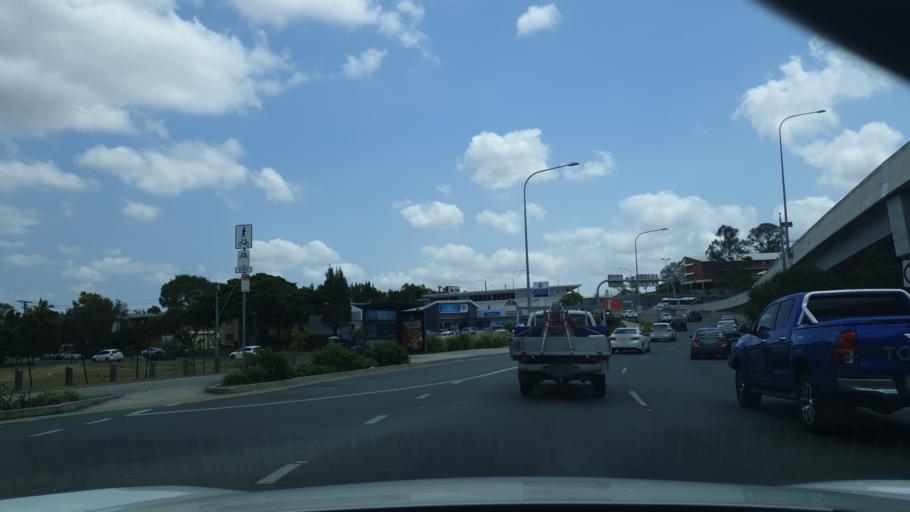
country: AU
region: Queensland
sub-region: Brisbane
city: Gordon Park
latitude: -27.4123
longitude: 153.0335
